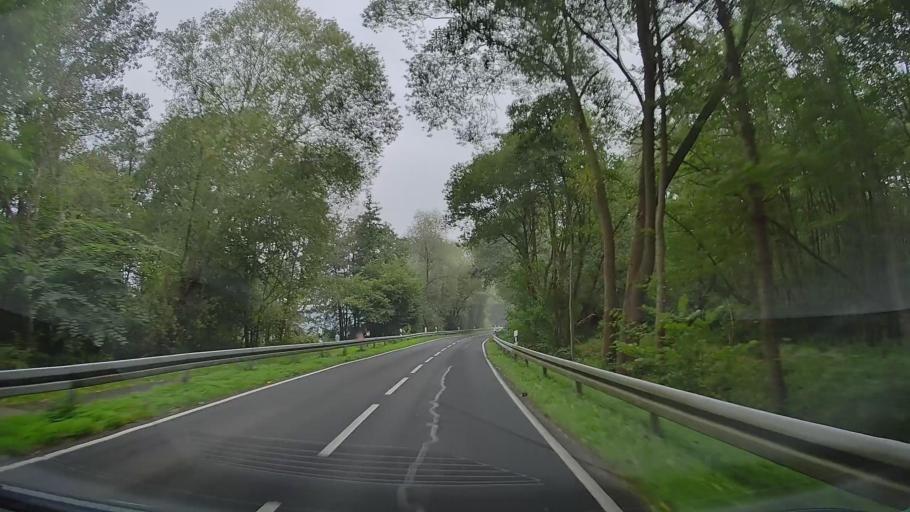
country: DE
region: Mecklenburg-Vorpommern
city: Neubukow
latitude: 54.0876
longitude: 11.6317
